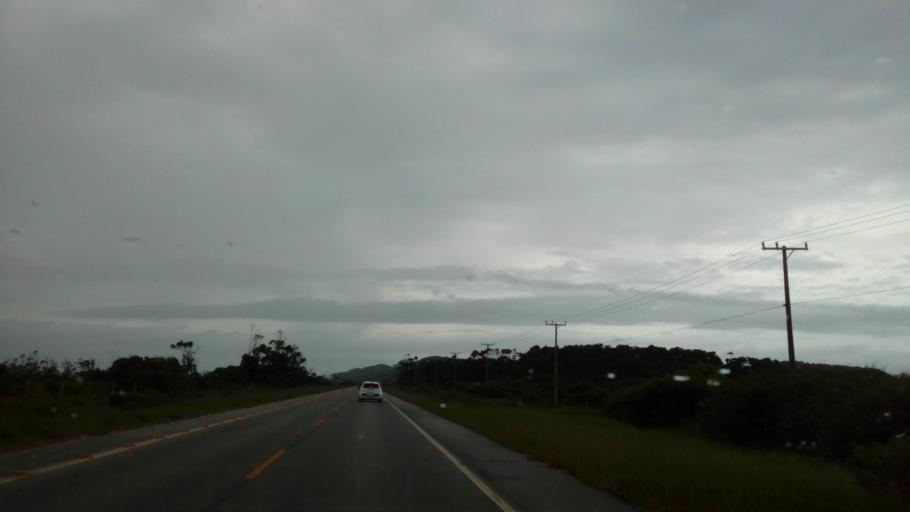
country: BR
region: Santa Catarina
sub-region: Laguna
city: Laguna
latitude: -28.5350
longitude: -48.7841
